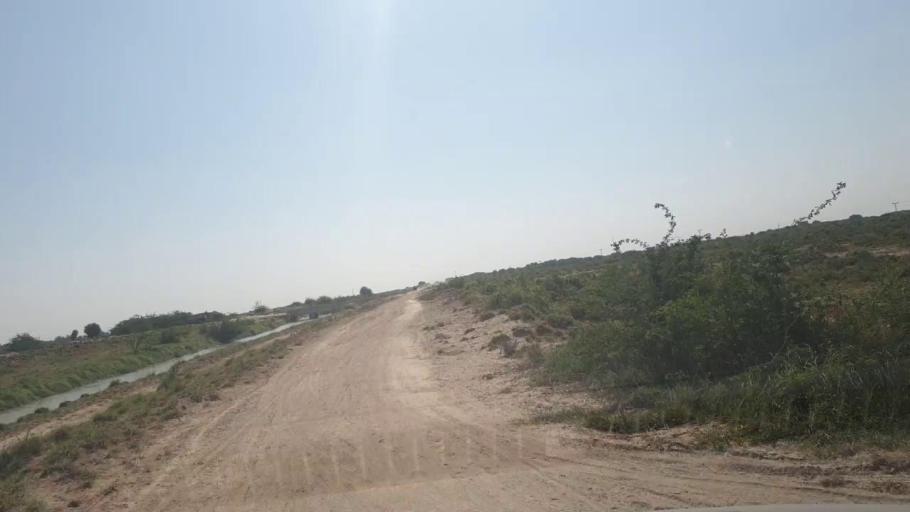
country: PK
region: Sindh
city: Digri
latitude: 24.9229
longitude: 69.1645
